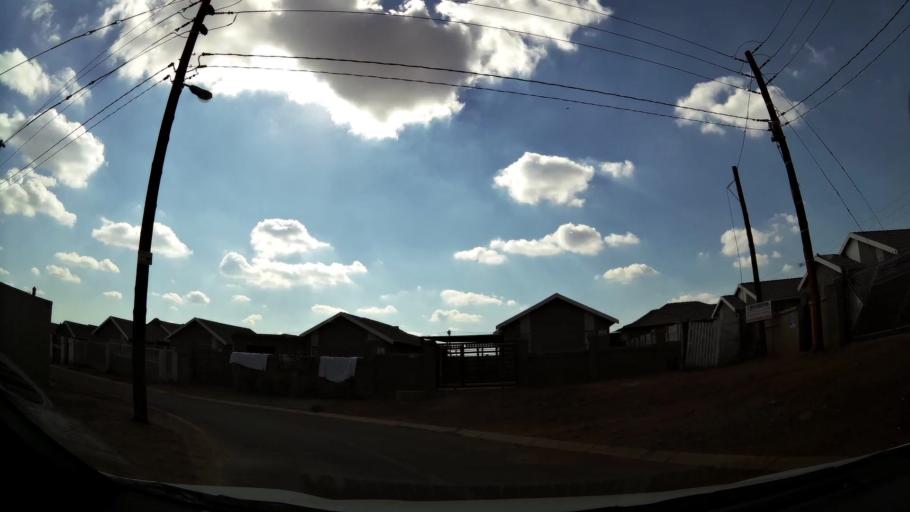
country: ZA
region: Gauteng
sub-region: City of Tshwane Metropolitan Municipality
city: Cullinan
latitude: -25.6897
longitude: 28.4085
